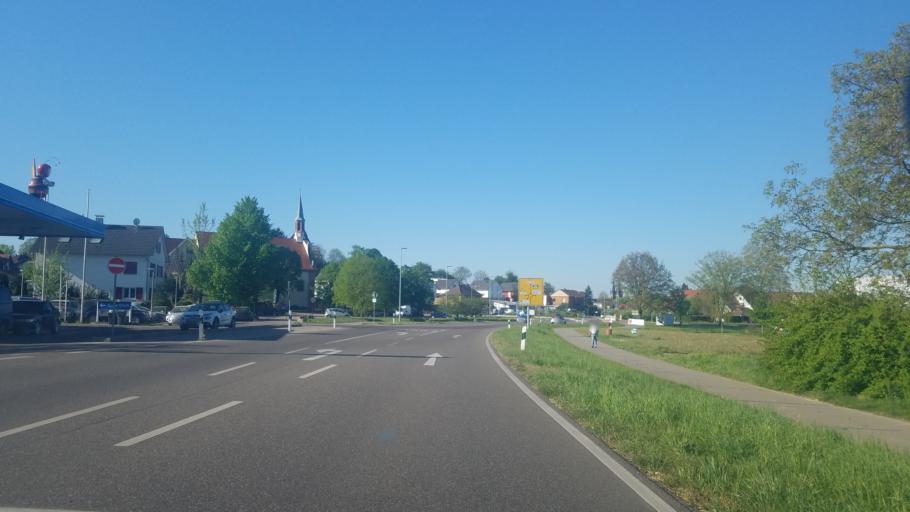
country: DE
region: Baden-Wuerttemberg
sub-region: Karlsruhe Region
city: Ottersweier
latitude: 48.6739
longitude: 8.1206
